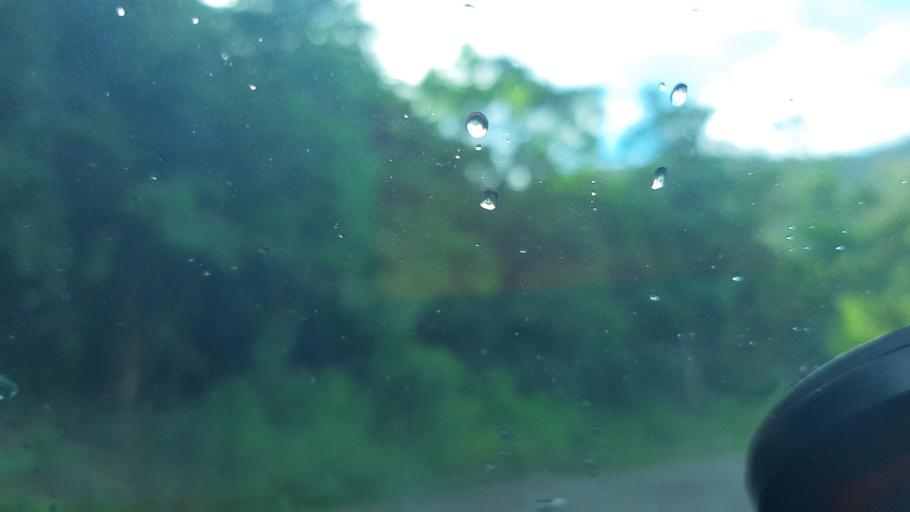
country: CO
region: Cundinamarca
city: Tenza
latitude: 5.0753
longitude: -73.4119
